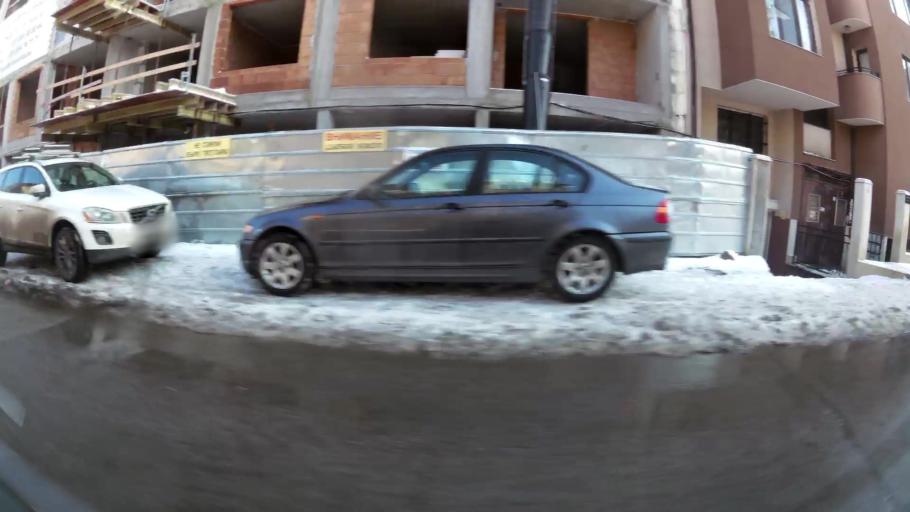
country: BG
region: Sofia-Capital
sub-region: Stolichna Obshtina
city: Sofia
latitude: 42.6692
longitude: 23.3627
